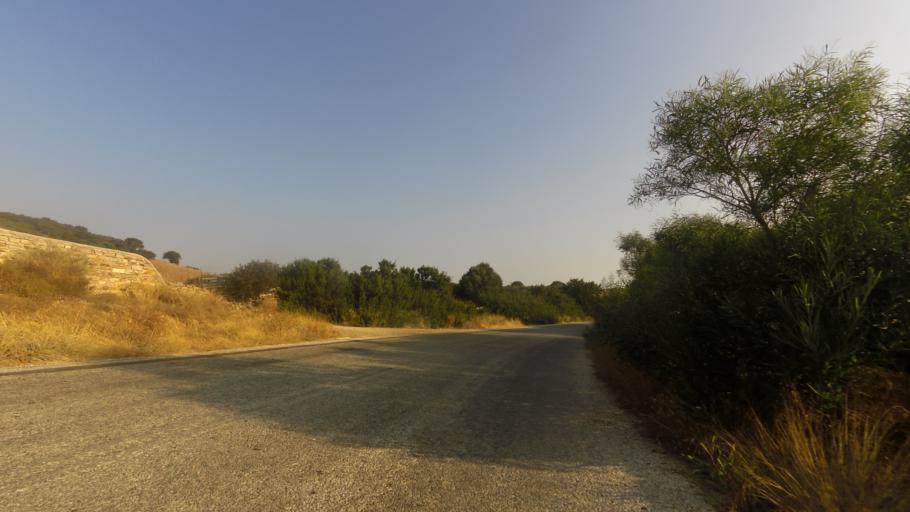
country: GR
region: South Aegean
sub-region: Nomos Kykladon
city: Antiparos
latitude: 36.9927
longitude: 25.0701
